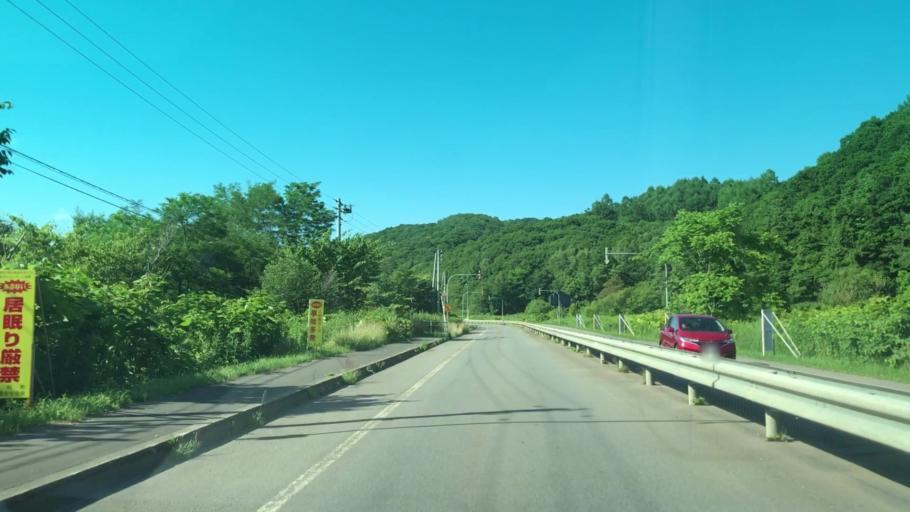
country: JP
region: Hokkaido
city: Iwanai
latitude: 42.9992
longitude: 140.6683
